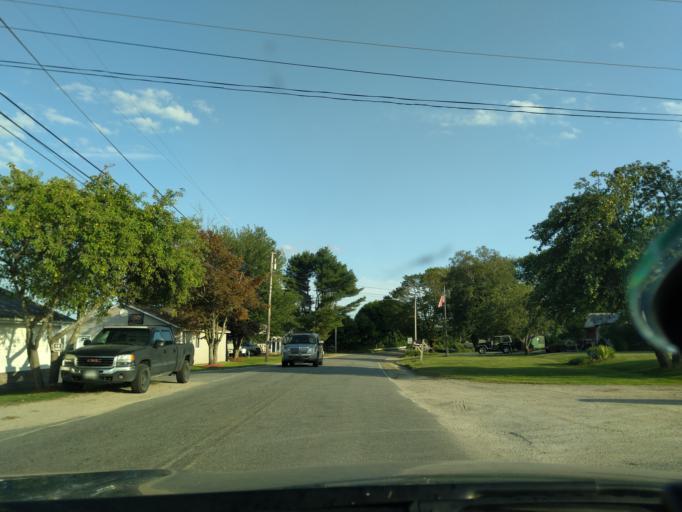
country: US
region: Maine
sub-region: Hancock County
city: Gouldsboro
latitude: 44.3889
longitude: -68.0398
